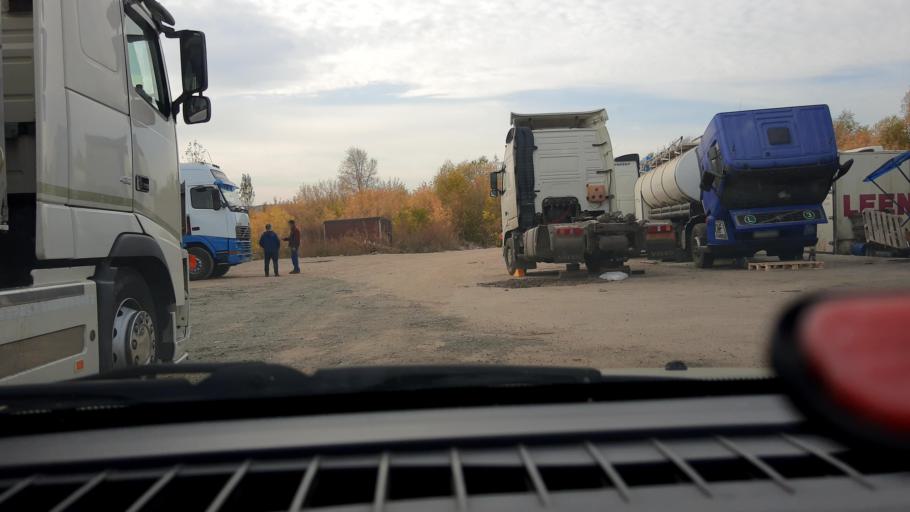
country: RU
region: Nizjnij Novgorod
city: Nizhniy Novgorod
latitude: 56.2639
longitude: 43.9524
